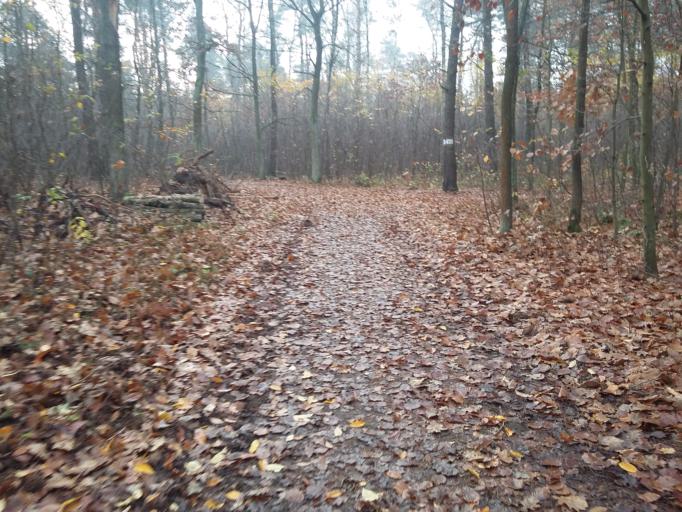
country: PL
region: Lodz Voivodeship
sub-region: Powiat pabianicki
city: Ksawerow
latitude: 51.7252
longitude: 19.3785
